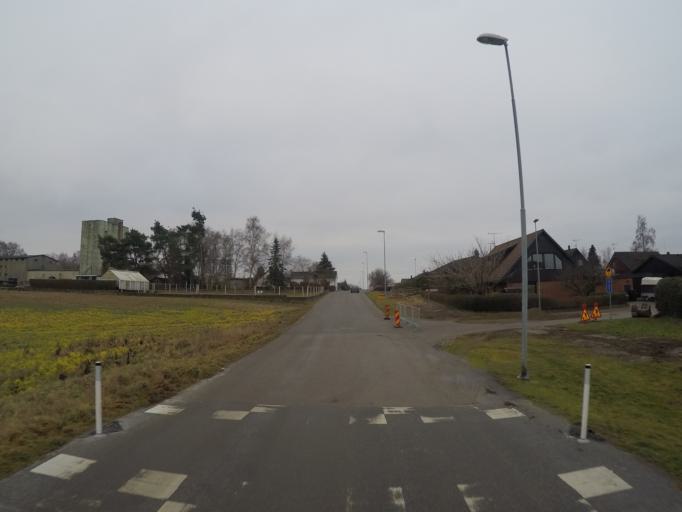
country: SE
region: Skane
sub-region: Eslovs Kommun
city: Eslov
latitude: 55.7547
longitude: 13.3728
